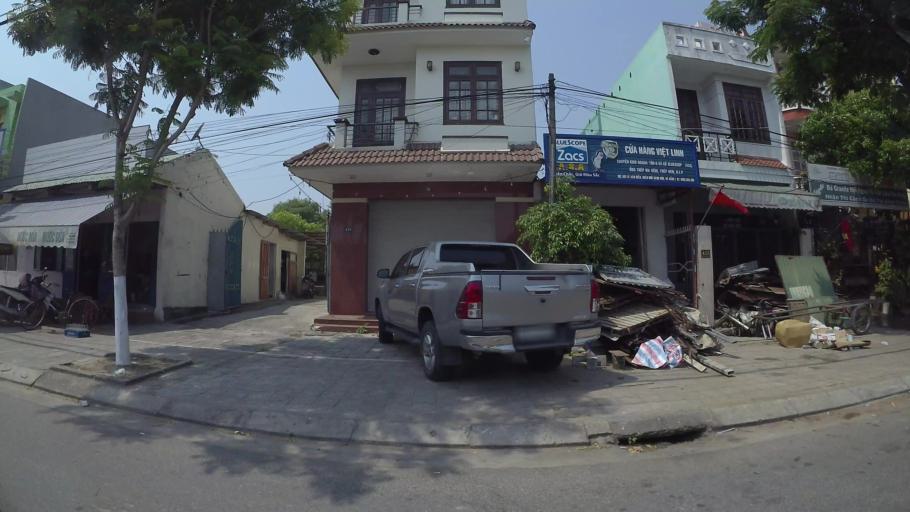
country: VN
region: Da Nang
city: Ngu Hanh Son
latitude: 16.0198
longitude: 108.2522
